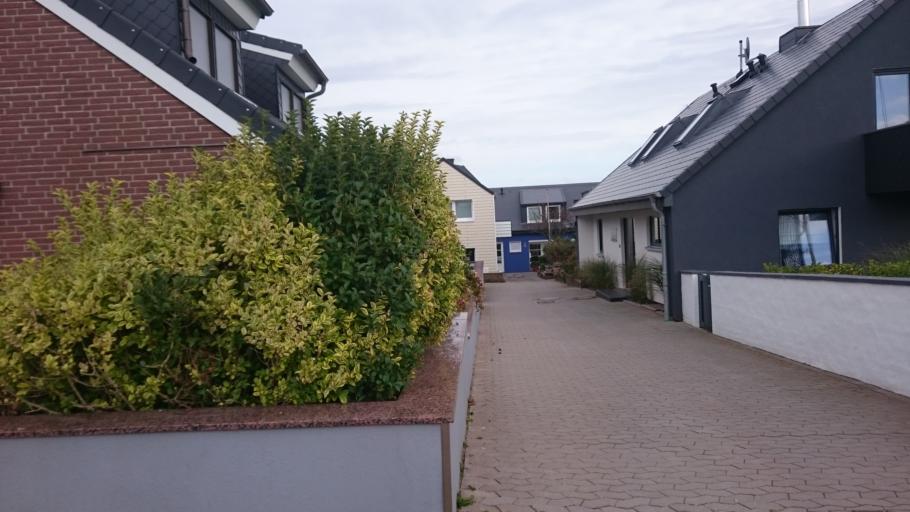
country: DE
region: Schleswig-Holstein
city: Helgoland
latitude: 54.1812
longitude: 7.8842
